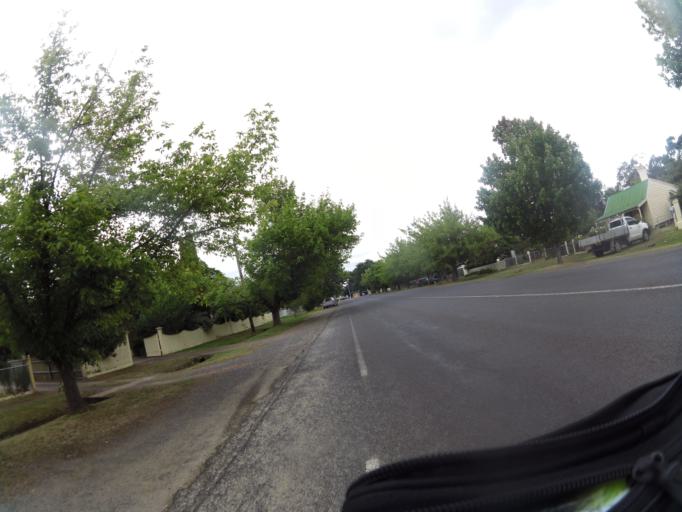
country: AU
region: Victoria
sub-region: Mount Alexander
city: Castlemaine
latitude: -37.0679
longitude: 144.2121
